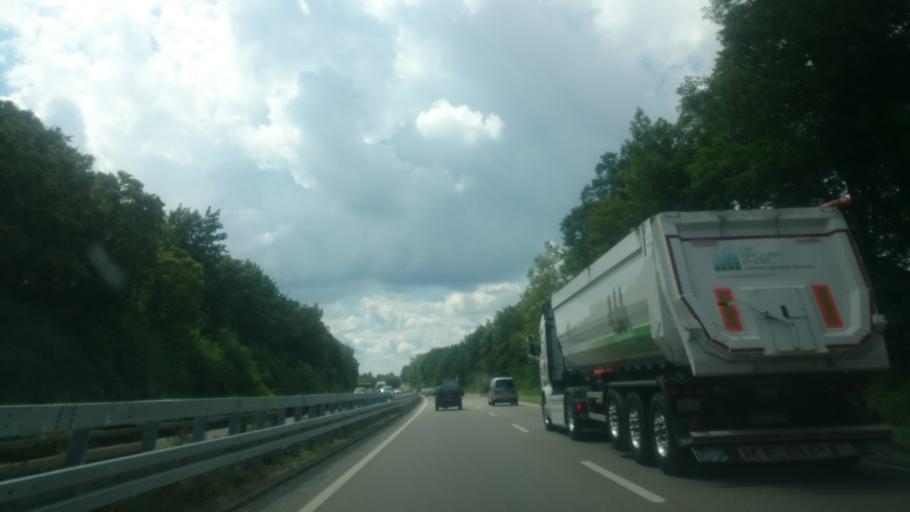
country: DE
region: Bavaria
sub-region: Swabia
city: Gersthofen
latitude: 48.4299
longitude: 10.8672
